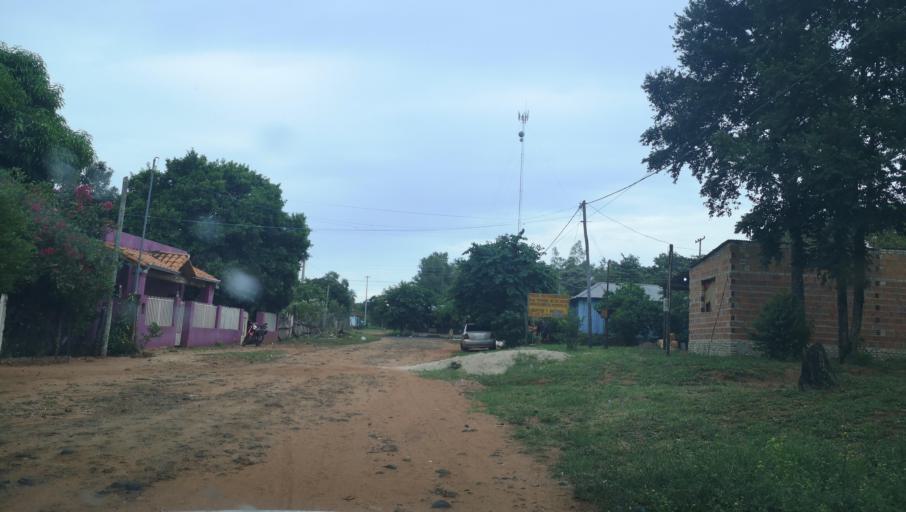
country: PY
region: San Pedro
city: Capiibary
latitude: -24.7255
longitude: -56.0137
